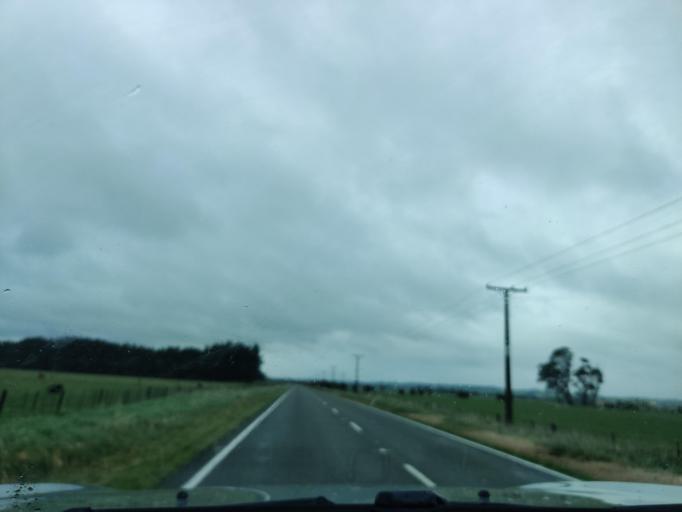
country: NZ
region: Hawke's Bay
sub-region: Hastings District
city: Hastings
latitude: -40.0091
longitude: 176.3798
